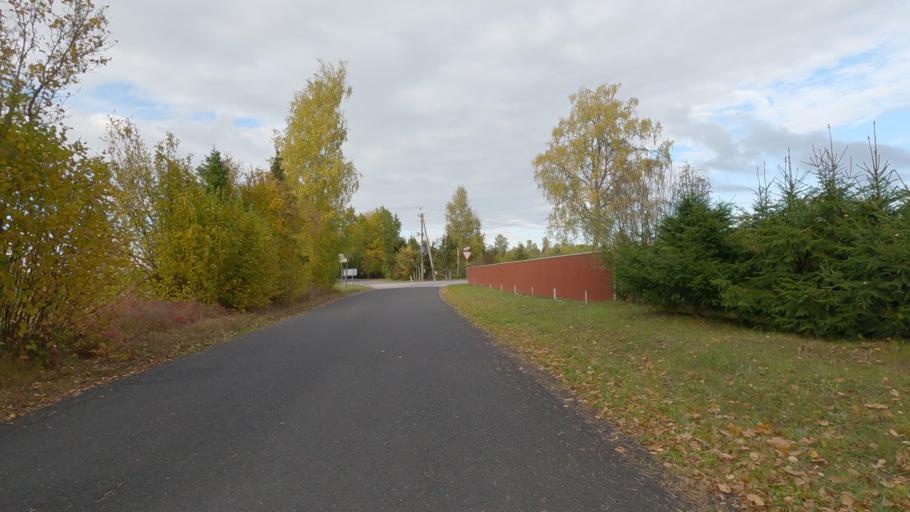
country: EE
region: Raplamaa
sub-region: Rapla vald
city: Rapla
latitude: 58.9789
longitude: 24.7849
